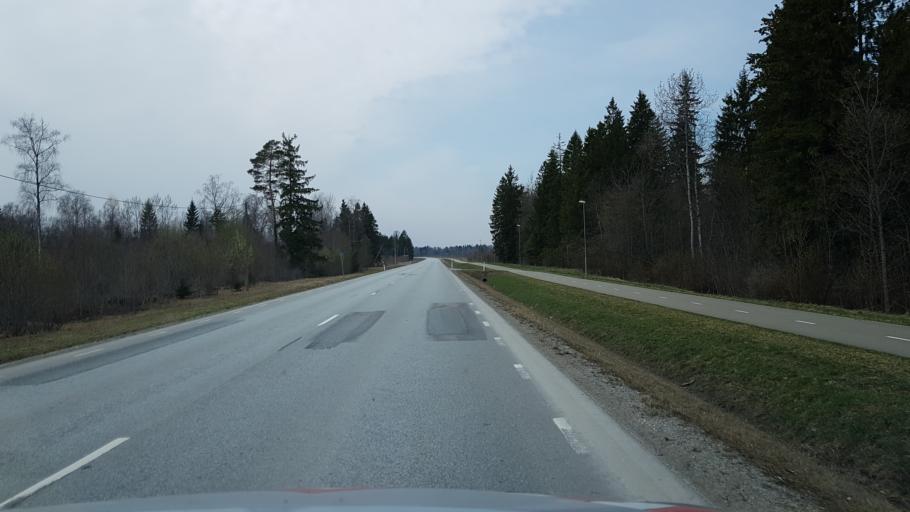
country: EE
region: Ida-Virumaa
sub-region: Kivioli linn
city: Kivioli
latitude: 59.3550
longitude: 26.8872
